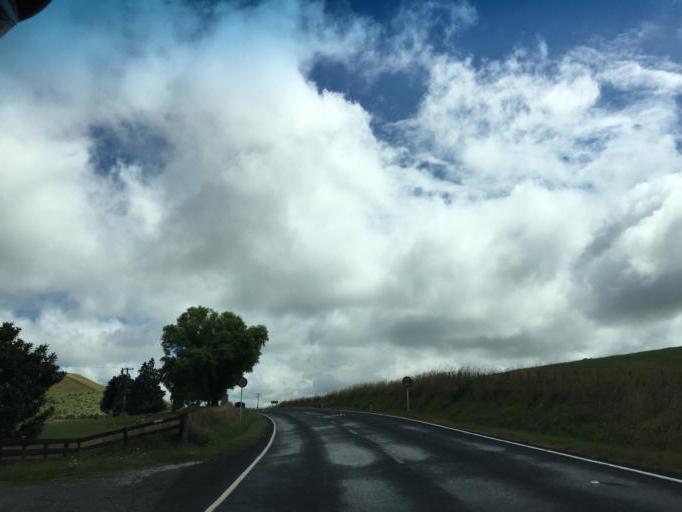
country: NZ
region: Hawke's Bay
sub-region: Napier City
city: Napier
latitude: -39.1330
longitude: 177.0010
